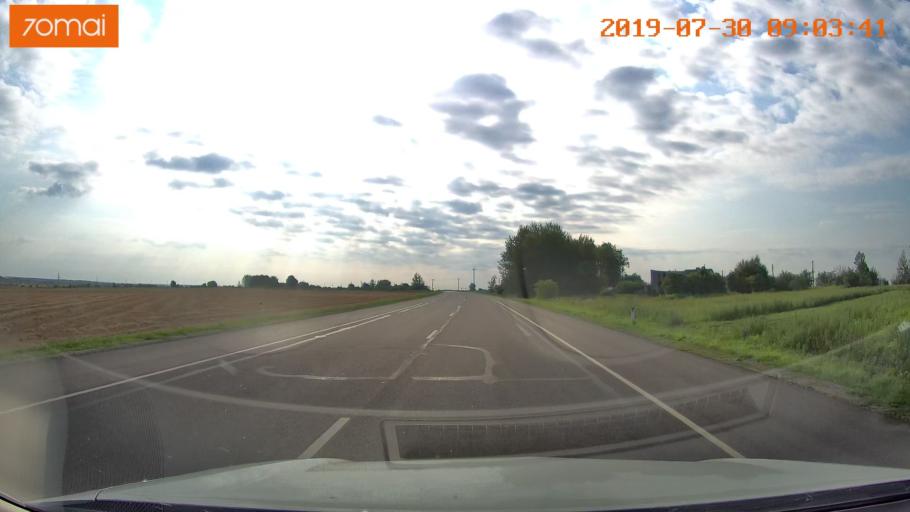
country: RU
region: Kaliningrad
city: Gusev
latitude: 54.6065
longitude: 22.2602
